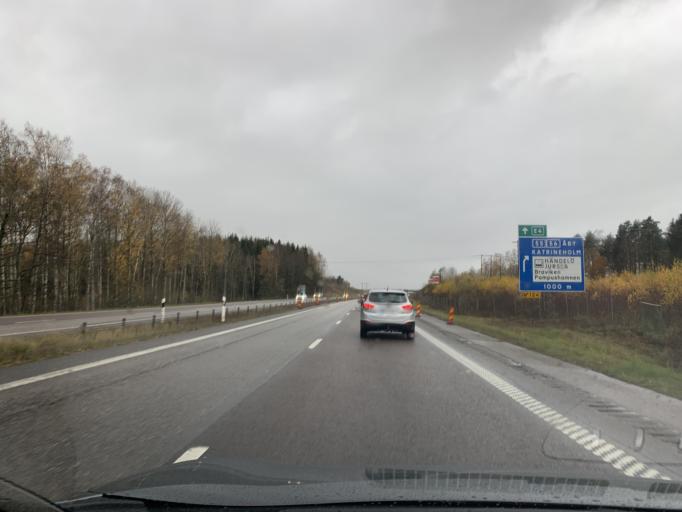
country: SE
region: OEstergoetland
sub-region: Norrkopings Kommun
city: Jursla
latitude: 58.6556
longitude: 16.1905
